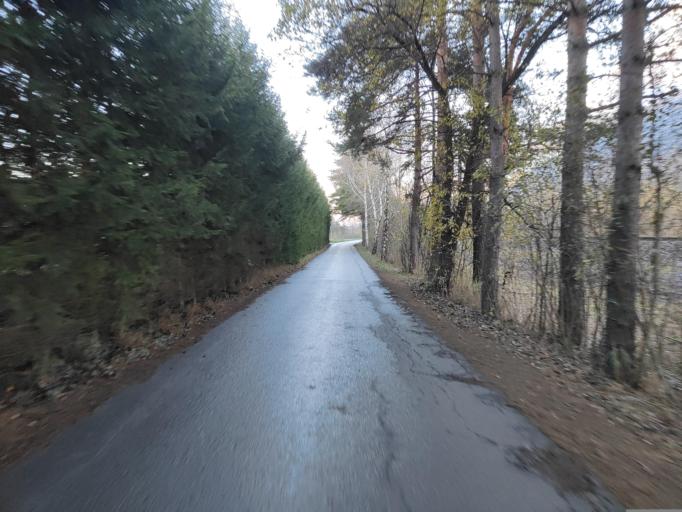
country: LI
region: Planken
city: Planken
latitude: 47.1843
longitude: 9.5238
